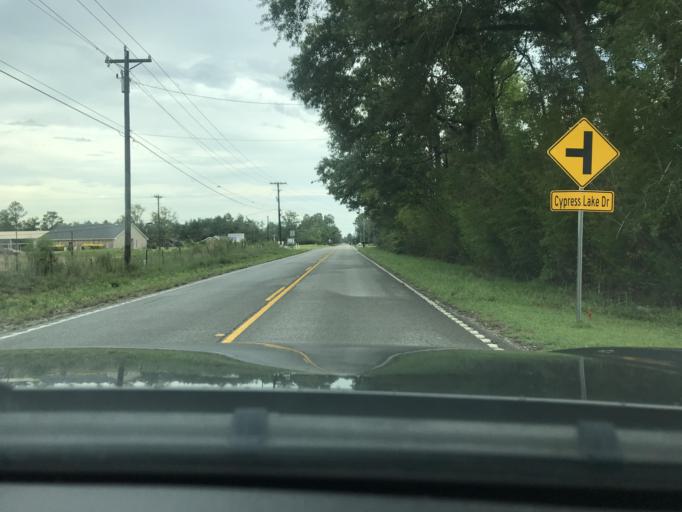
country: US
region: Louisiana
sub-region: Calcasieu Parish
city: Moss Bluff
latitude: 30.3215
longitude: -93.2582
